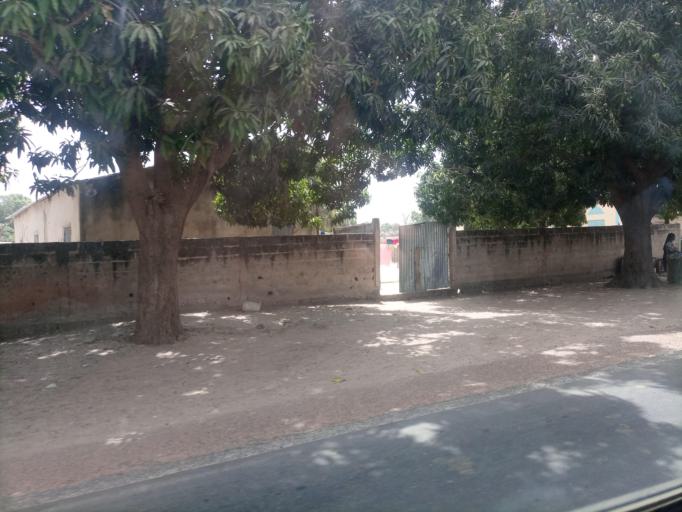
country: SN
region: Fatick
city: Sokone
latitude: 13.7141
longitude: -16.4262
